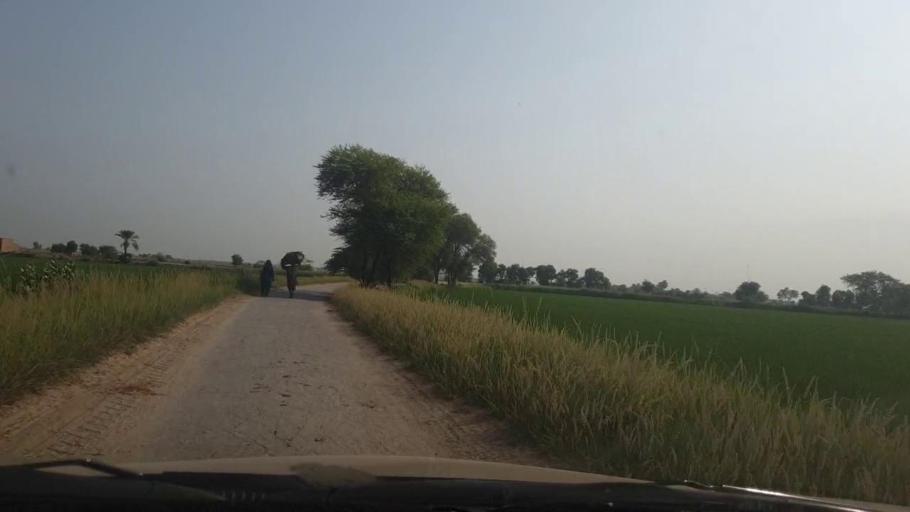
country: PK
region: Sindh
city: Larkana
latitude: 27.5882
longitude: 68.1882
